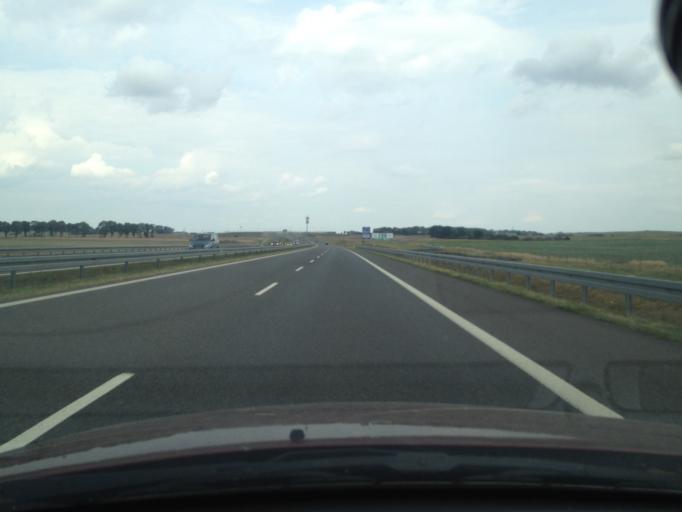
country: PL
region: West Pomeranian Voivodeship
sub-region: Powiat pyrzycki
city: Kozielice
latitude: 53.0396
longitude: 14.8654
